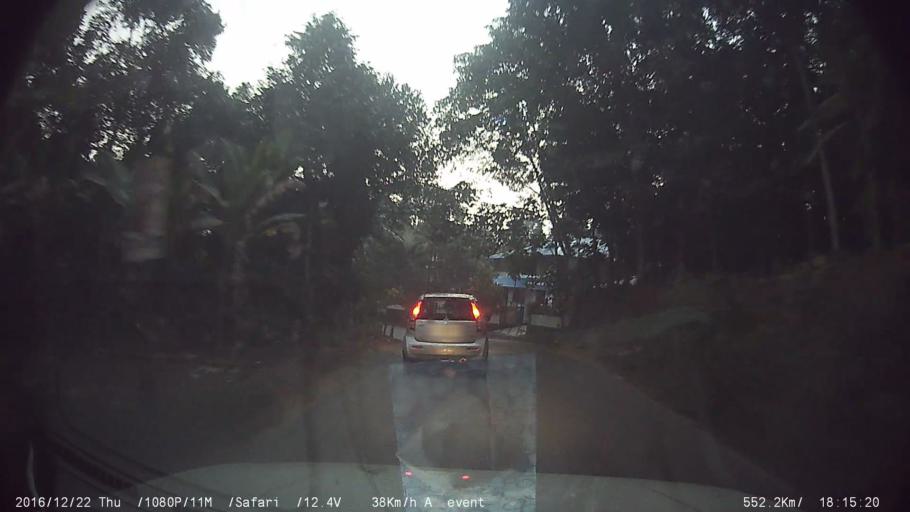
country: IN
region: Kerala
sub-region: Kottayam
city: Palackattumala
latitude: 9.7738
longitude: 76.6123
